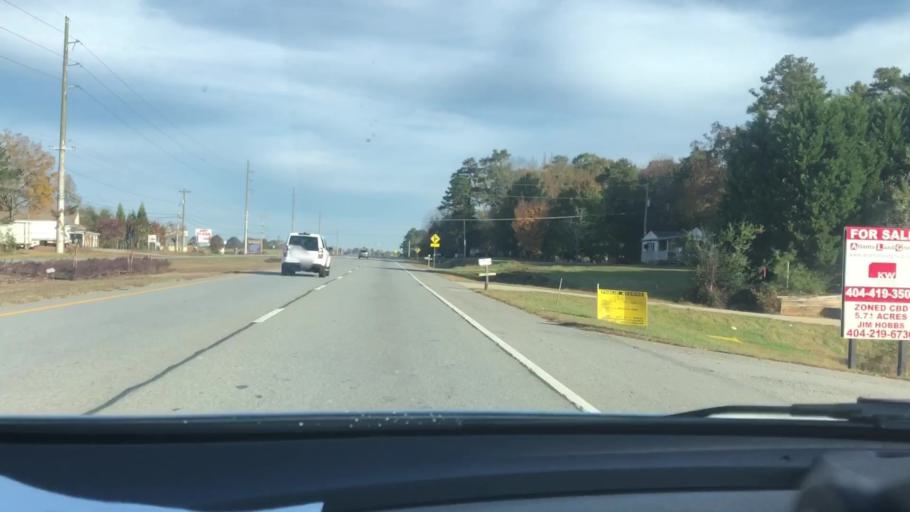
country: US
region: Georgia
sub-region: Fulton County
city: Johns Creek
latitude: 34.1066
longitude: -84.1766
